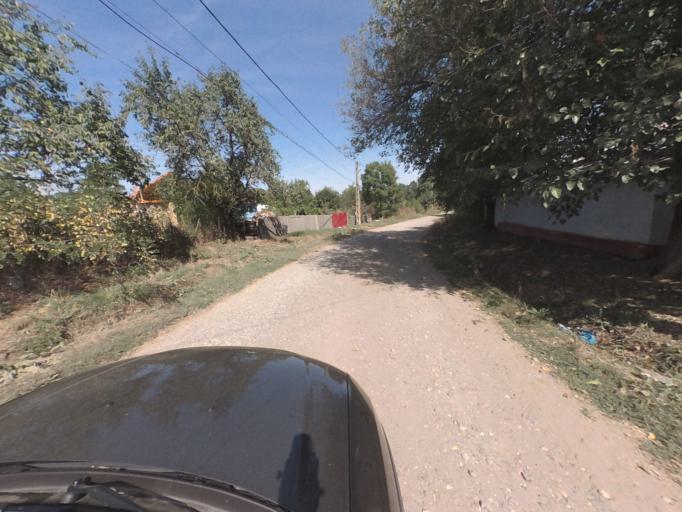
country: RO
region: Vaslui
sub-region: Comuna Deleni
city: Deleni
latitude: 46.5326
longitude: 27.7531
